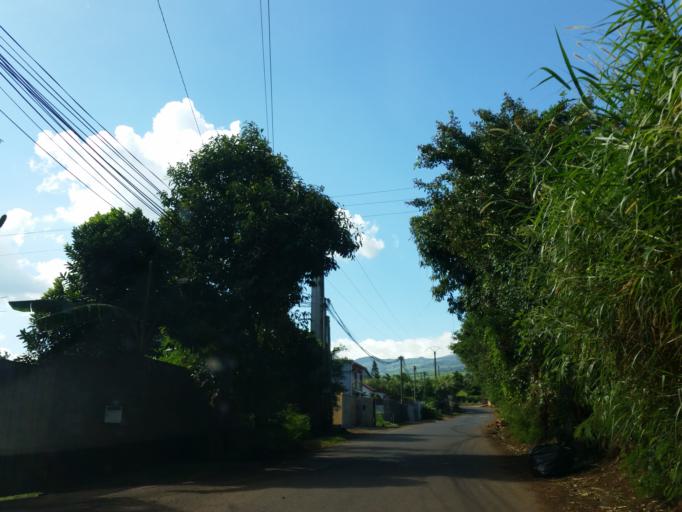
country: RE
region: Reunion
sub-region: Reunion
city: Saint-Pierre
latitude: -21.3260
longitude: 55.4982
